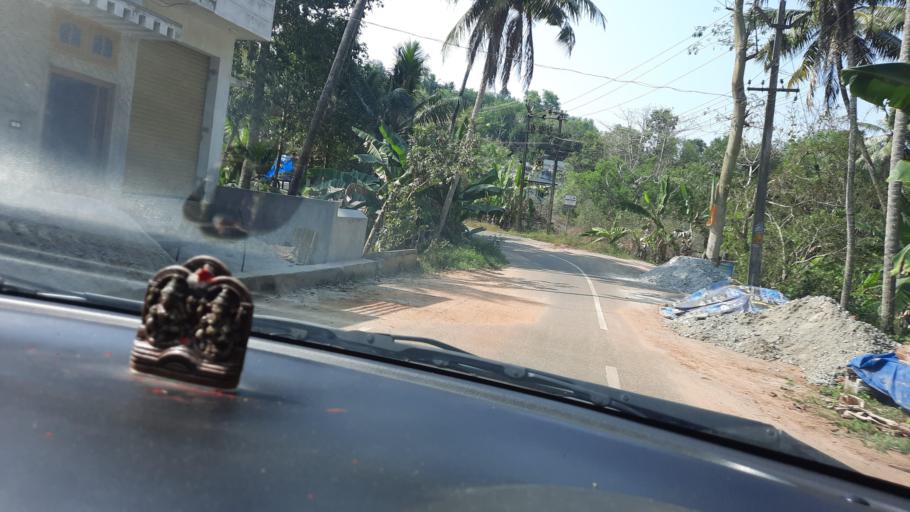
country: IN
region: Kerala
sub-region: Thiruvananthapuram
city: Nedumangad
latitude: 8.5906
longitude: 76.9264
